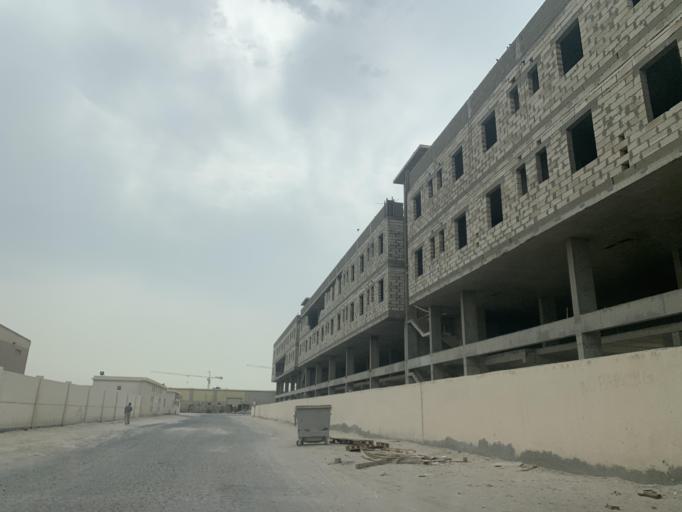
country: BH
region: Northern
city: Madinat `Isa
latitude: 26.1781
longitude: 50.5087
